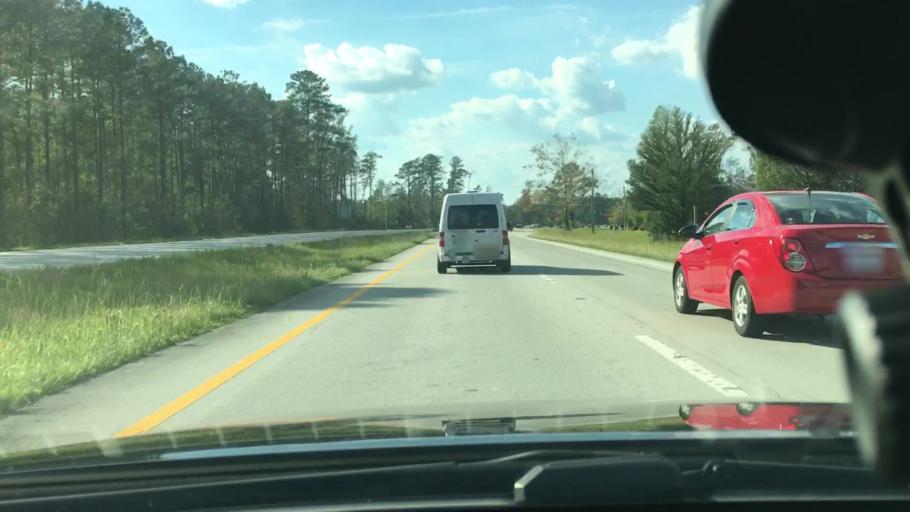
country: US
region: North Carolina
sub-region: Craven County
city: Neuse Forest
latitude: 34.9677
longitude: -76.9663
